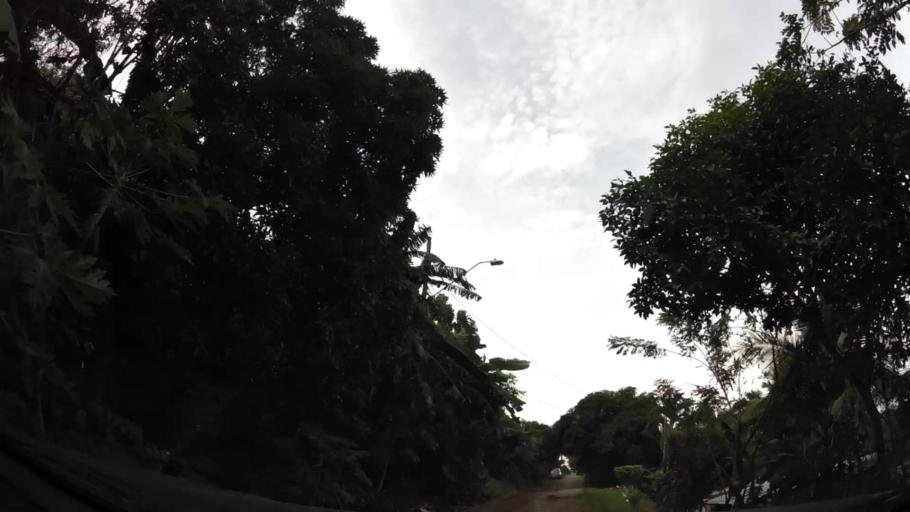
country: PA
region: Panama
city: Guadalupe
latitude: 8.8589
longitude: -79.8143
